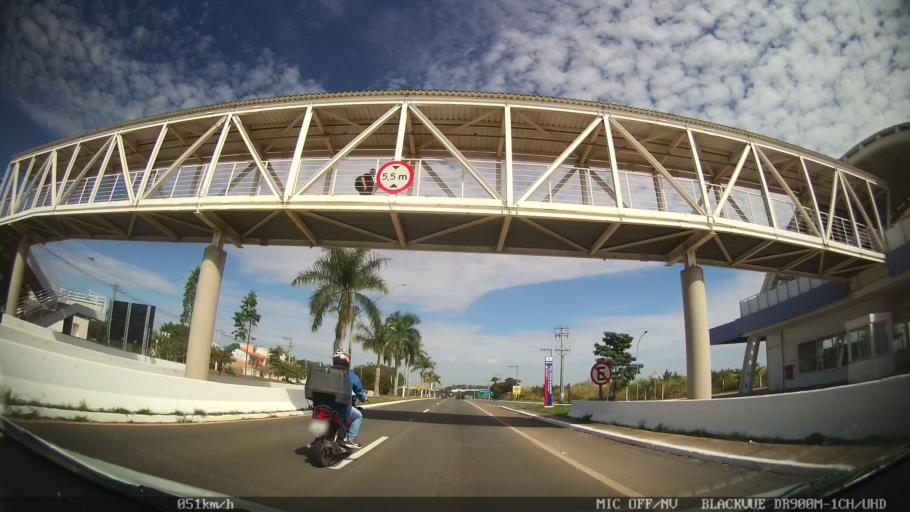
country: BR
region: Sao Paulo
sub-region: Santa Barbara D'Oeste
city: Santa Barbara d'Oeste
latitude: -22.7659
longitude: -47.4348
